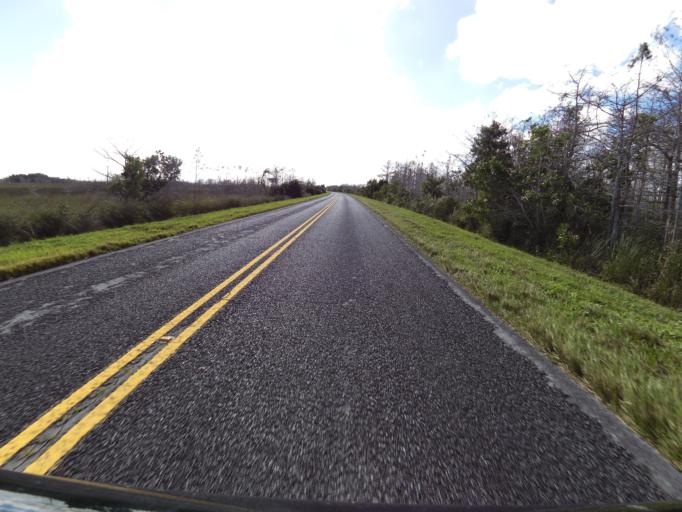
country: US
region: Florida
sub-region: Miami-Dade County
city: Florida City
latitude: 25.4226
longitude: -80.7763
